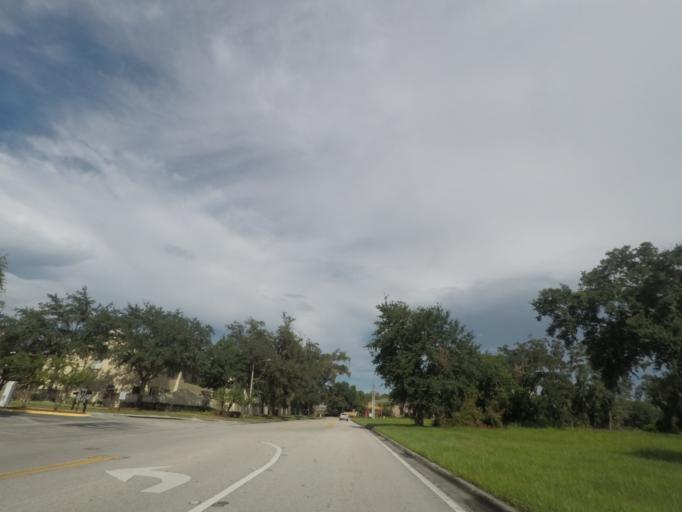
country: US
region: Florida
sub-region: Osceola County
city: Kissimmee
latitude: 28.3258
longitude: -81.4641
